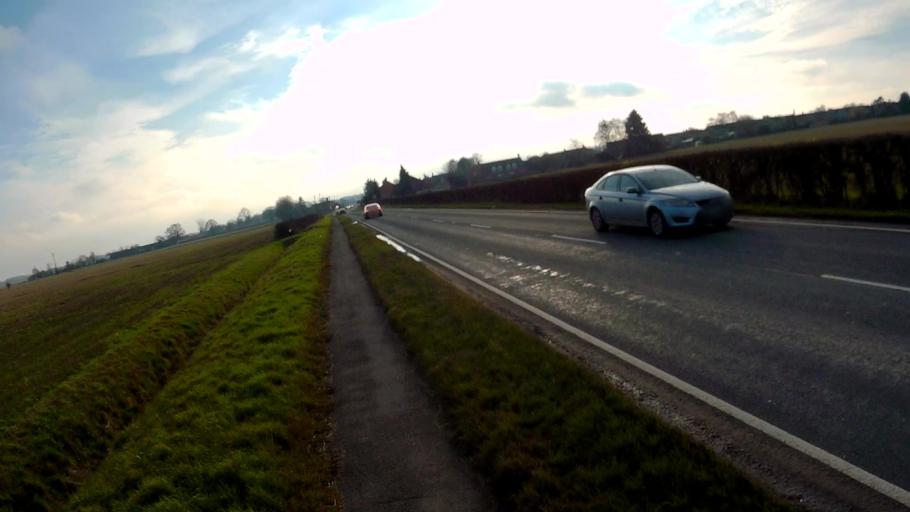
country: GB
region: England
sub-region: Lincolnshire
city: Bourne
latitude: 52.7480
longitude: -0.3698
